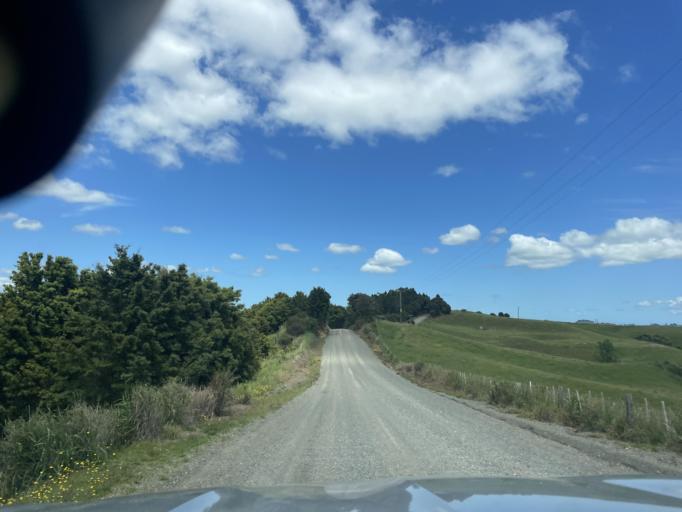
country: NZ
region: Auckland
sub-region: Auckland
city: Wellsford
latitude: -36.1596
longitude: 174.5367
